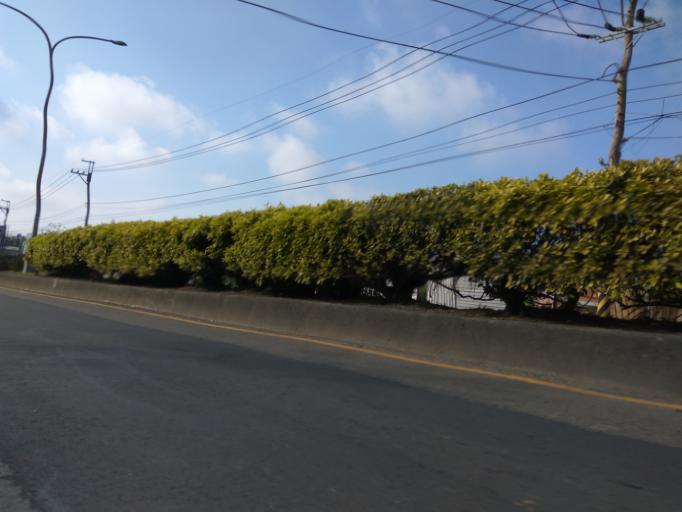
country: TW
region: Taiwan
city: Taoyuan City
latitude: 25.0683
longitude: 121.1915
